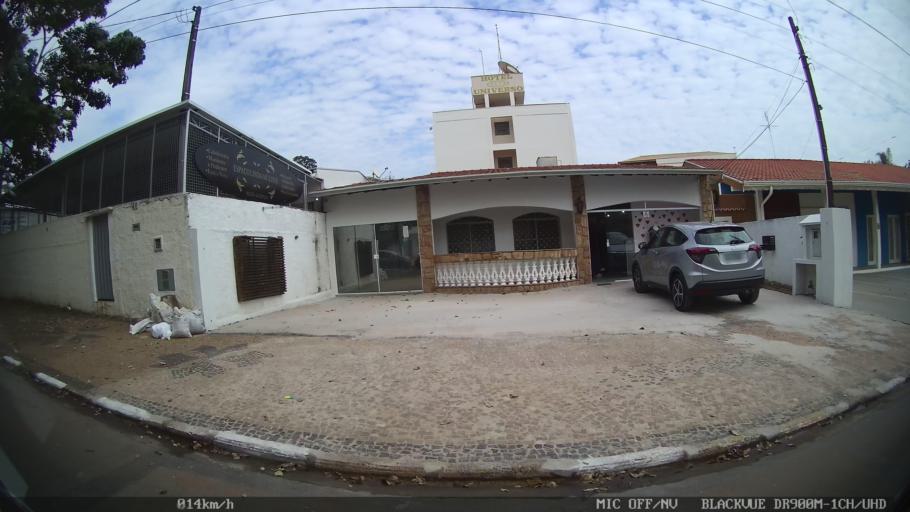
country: BR
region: Sao Paulo
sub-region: Paulinia
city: Paulinia
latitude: -22.7655
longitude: -47.1518
